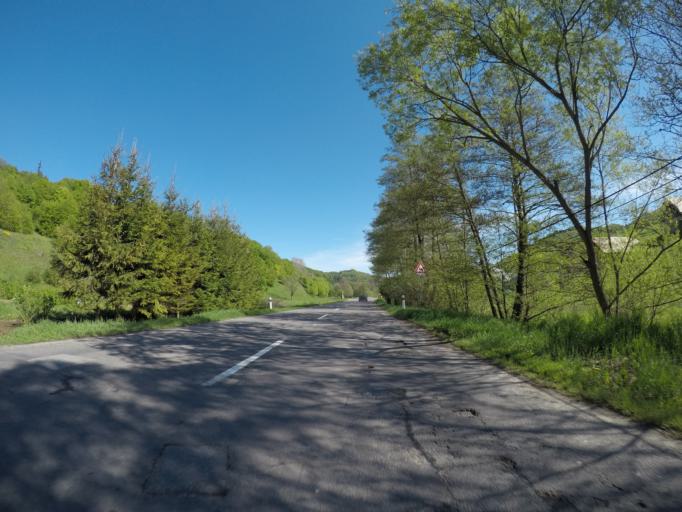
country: SK
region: Banskobystricky
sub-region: Okres Banska Bystrica
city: Banska Stiavnica
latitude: 48.4783
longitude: 18.9441
